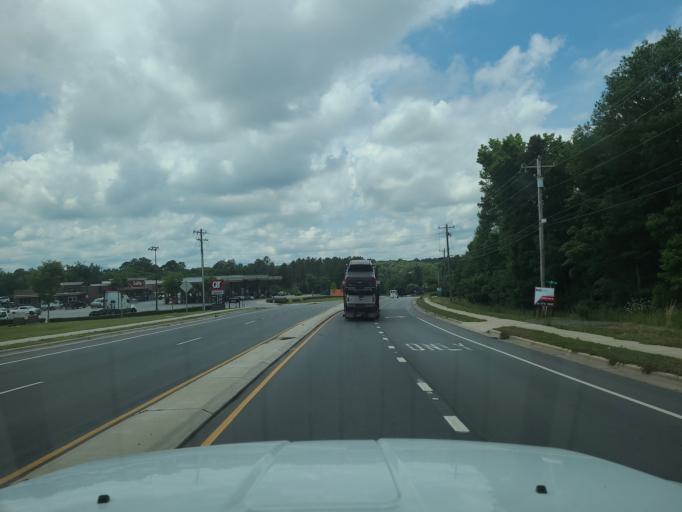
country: US
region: North Carolina
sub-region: Cabarrus County
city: Kannapolis
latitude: 35.4988
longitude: -80.5662
